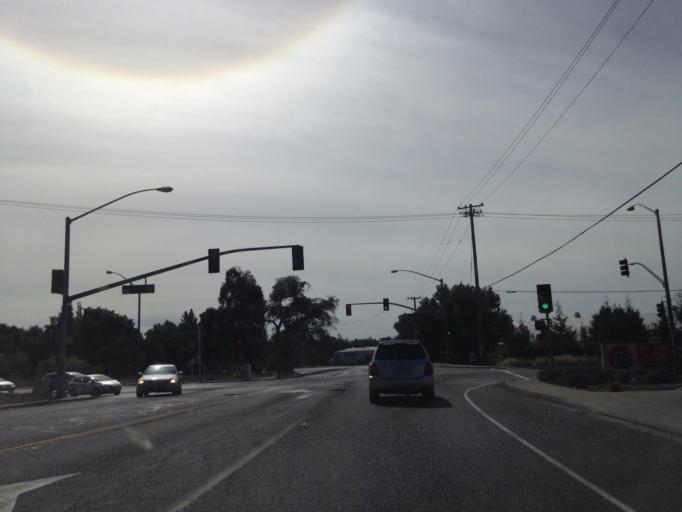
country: US
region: California
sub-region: Sonoma County
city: Graton
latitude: 38.4261
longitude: -122.8484
